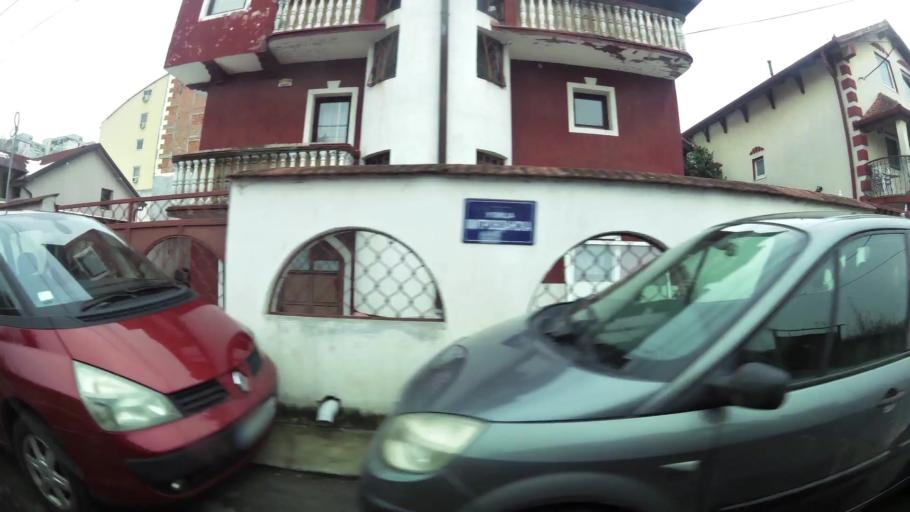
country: RS
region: Central Serbia
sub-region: Belgrade
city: Vozdovac
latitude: 44.7616
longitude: 20.4971
